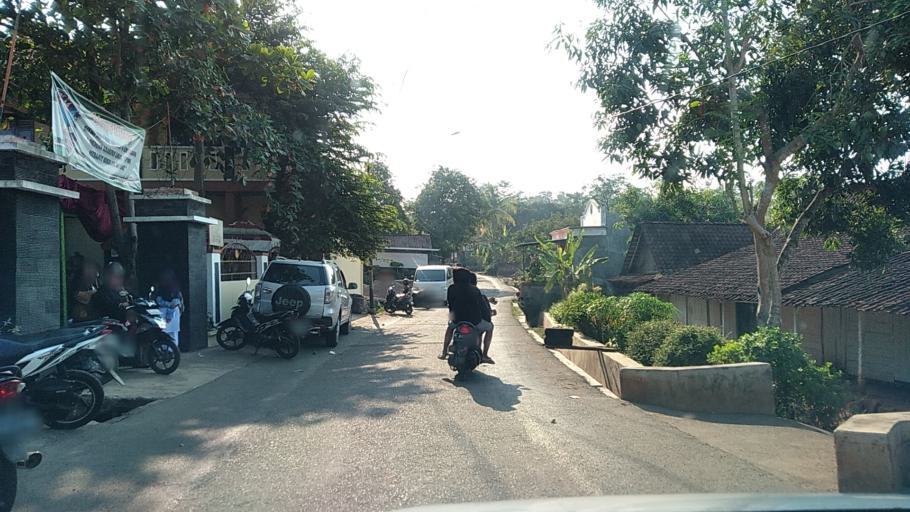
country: ID
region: Central Java
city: Semarang
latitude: -7.0386
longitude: 110.2930
